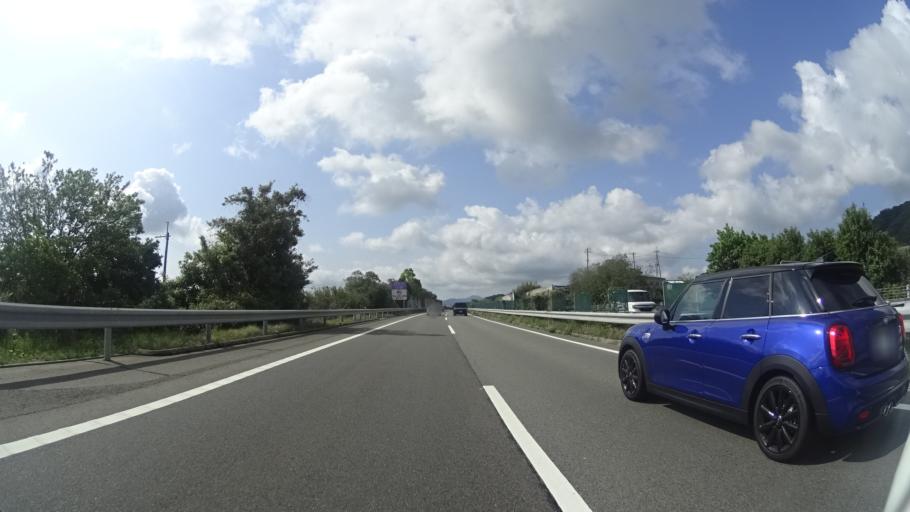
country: JP
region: Hyogo
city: Sumoto
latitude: 34.3800
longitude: 134.8610
